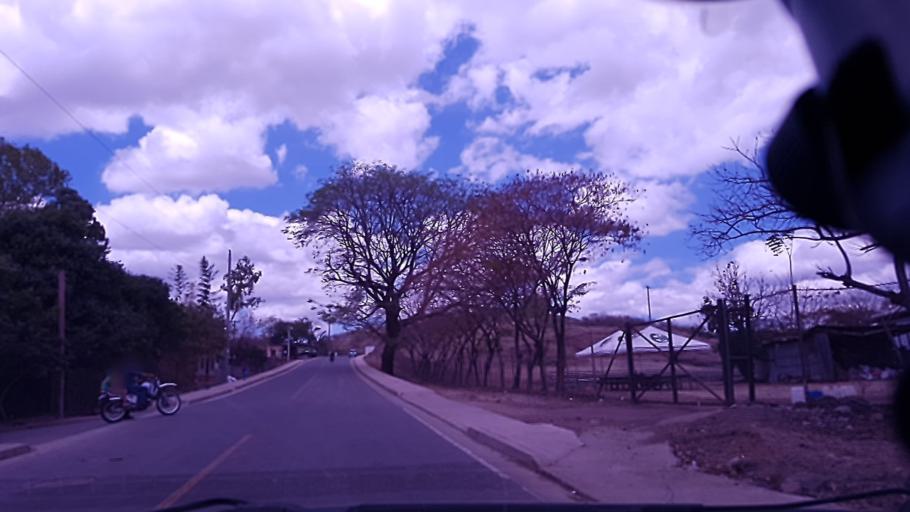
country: NI
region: Esteli
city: Condega
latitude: 13.3733
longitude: -86.3956
